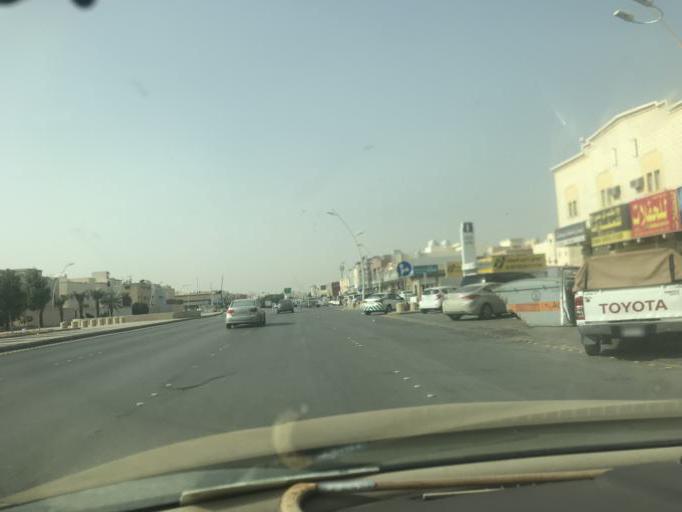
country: SA
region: Ar Riyad
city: Riyadh
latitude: 24.6806
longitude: 46.7993
